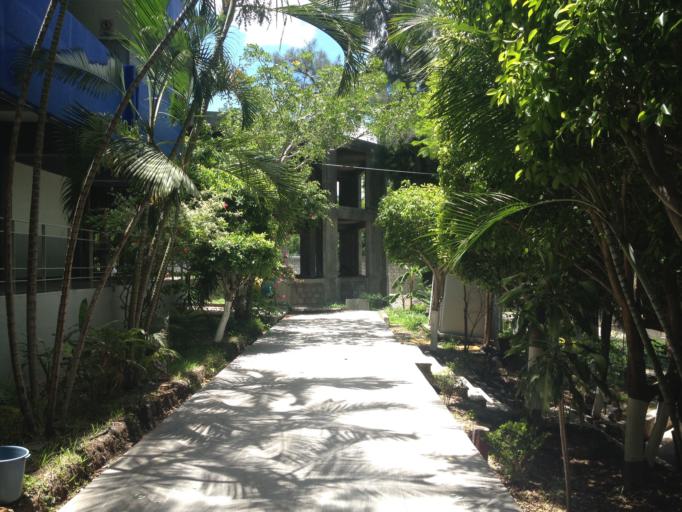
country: MX
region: Guerrero
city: Chilpancingo de los Bravos
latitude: 17.5364
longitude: -99.4953
